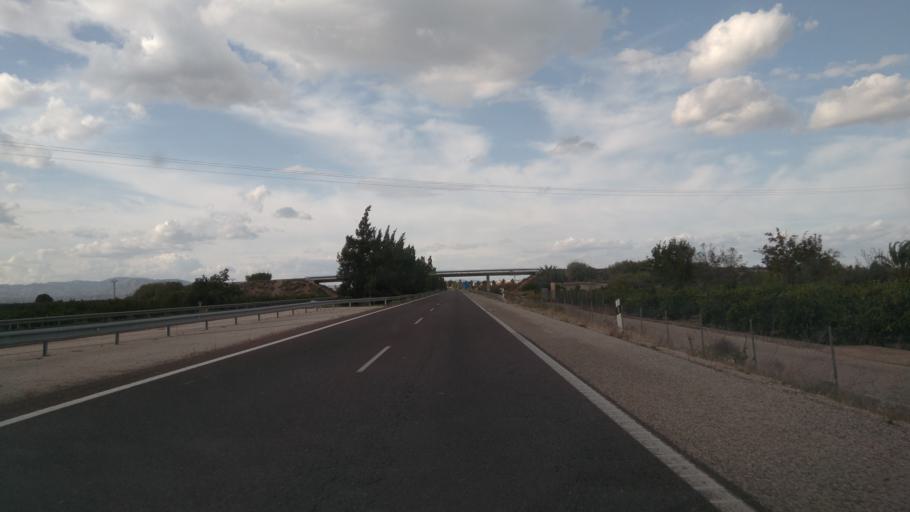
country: ES
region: Valencia
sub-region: Provincia de Valencia
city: Guadassuar
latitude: 39.1689
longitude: -0.4623
